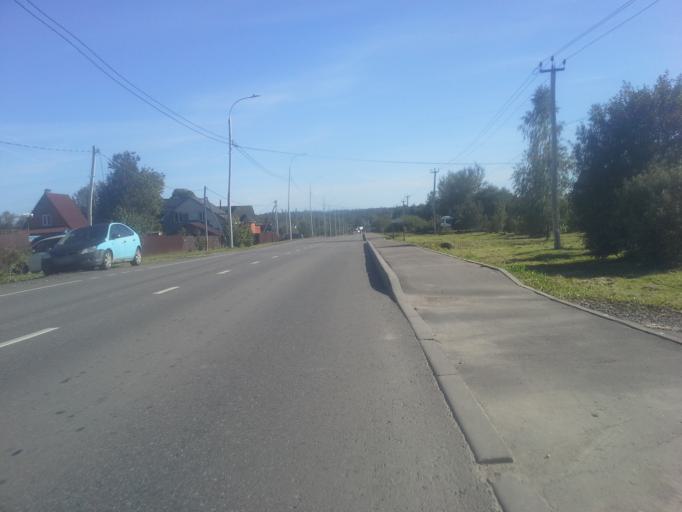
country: RU
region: Moskovskaya
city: Selyatino
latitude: 55.4154
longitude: 37.0110
